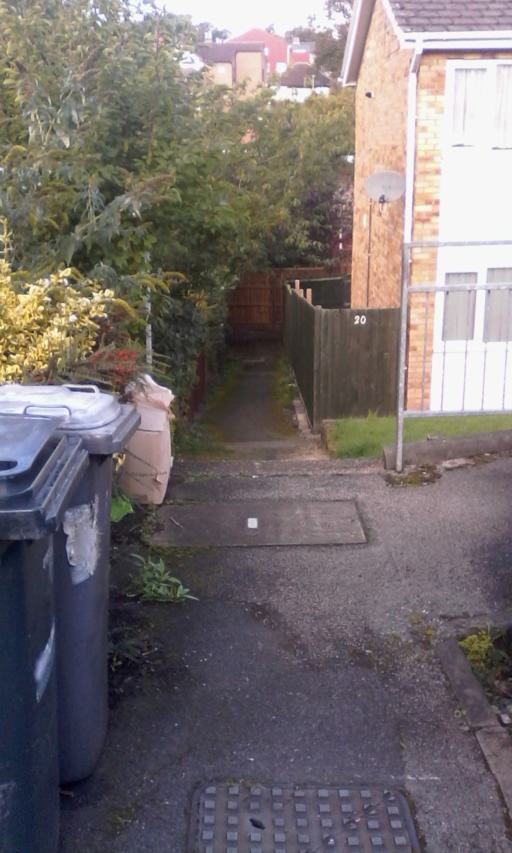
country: GB
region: England
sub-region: Nottinghamshire
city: Arnold
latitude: 52.9789
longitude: -1.1181
